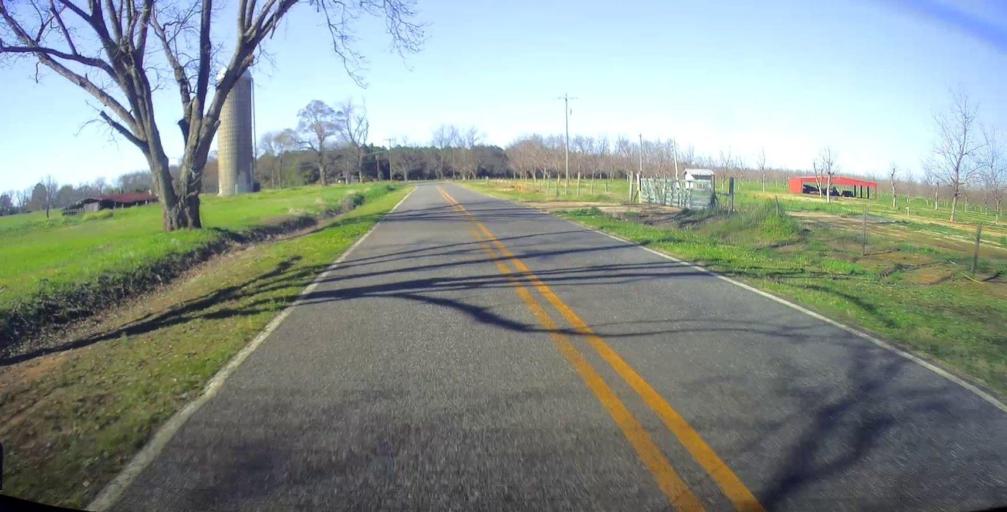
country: US
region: Georgia
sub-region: Peach County
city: Fort Valley
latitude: 32.6203
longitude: -83.8529
